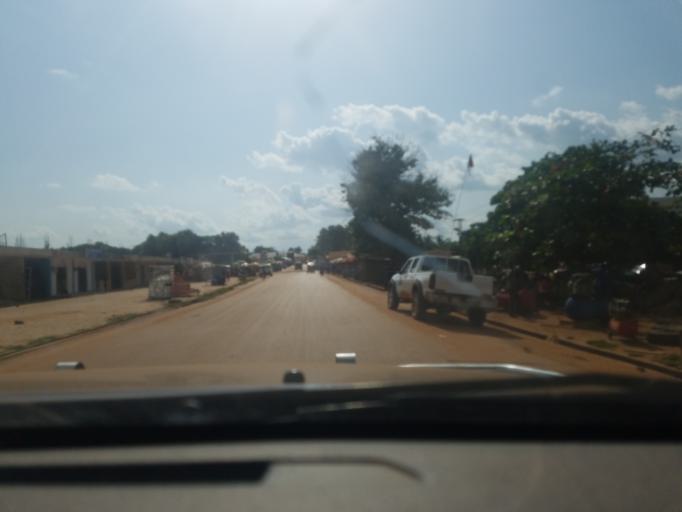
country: GH
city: Duayaw Nkwanta
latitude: 6.9785
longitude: -2.3833
